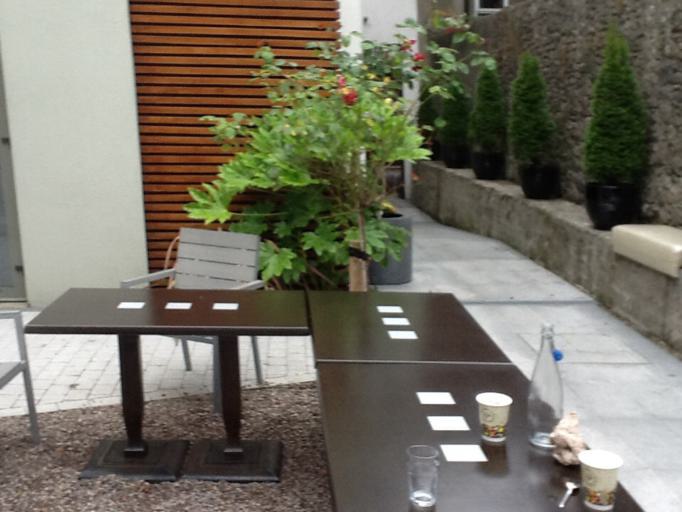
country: IE
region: Leinster
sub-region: Kilkenny
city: Kilkenny
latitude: 52.6497
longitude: -7.2512
